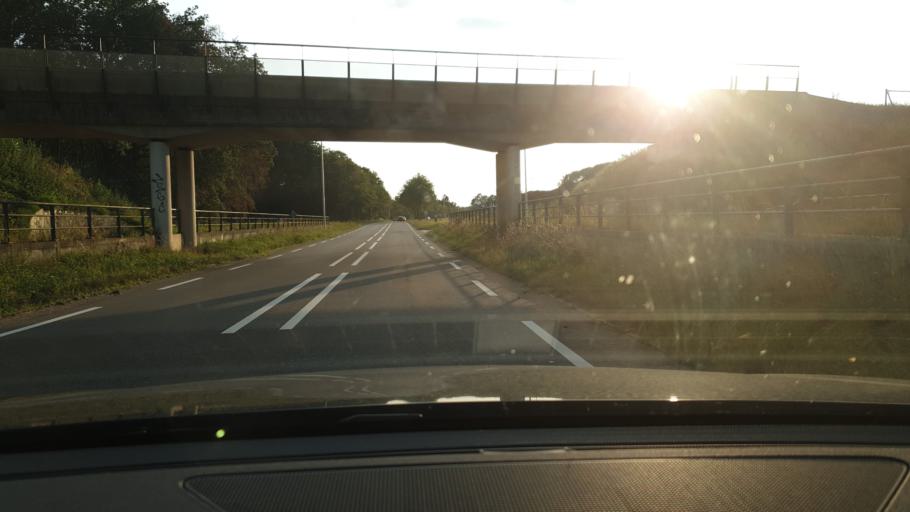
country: NL
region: North Brabant
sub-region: Gemeente Cuijk
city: Cuijk
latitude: 51.6924
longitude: 5.8997
